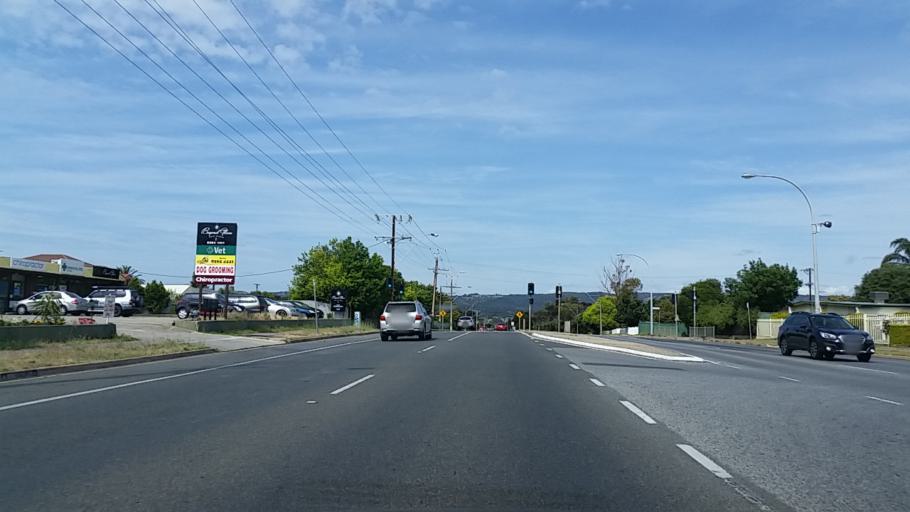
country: AU
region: South Australia
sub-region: Tea Tree Gully
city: Modbury
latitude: -34.8293
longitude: 138.6674
